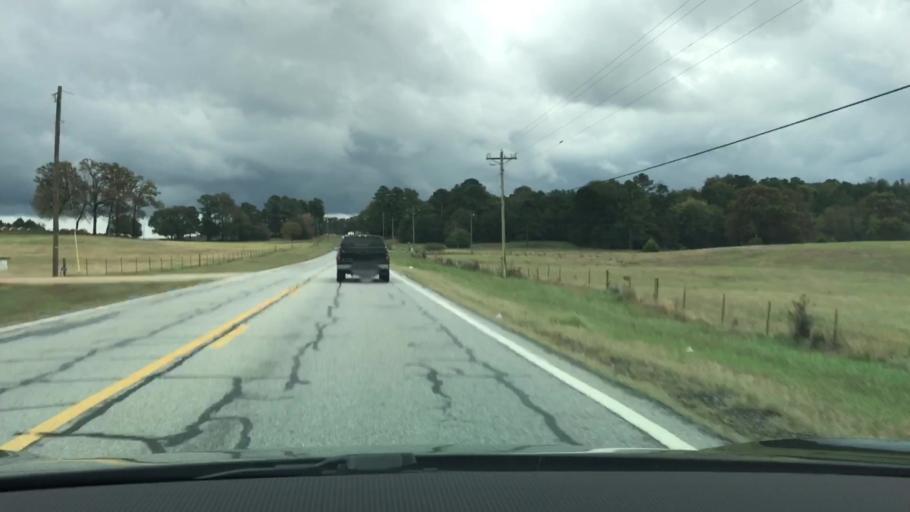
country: US
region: Georgia
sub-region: Oconee County
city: Watkinsville
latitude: 33.7940
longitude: -83.3271
